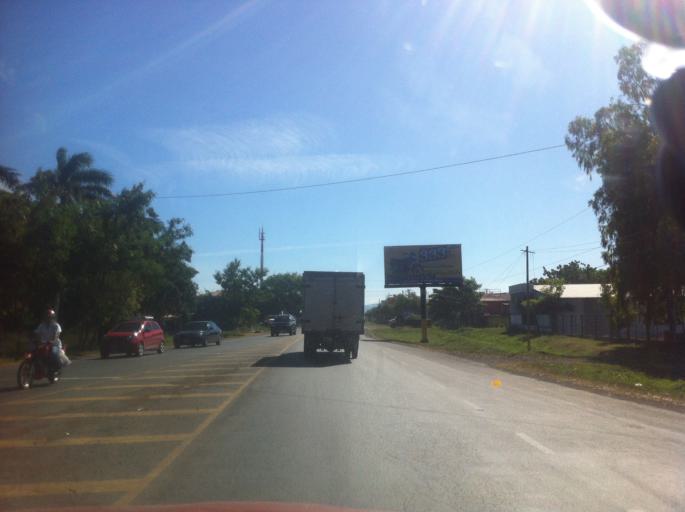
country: NI
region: Managua
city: Tipitapa
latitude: 12.1939
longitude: -86.1048
